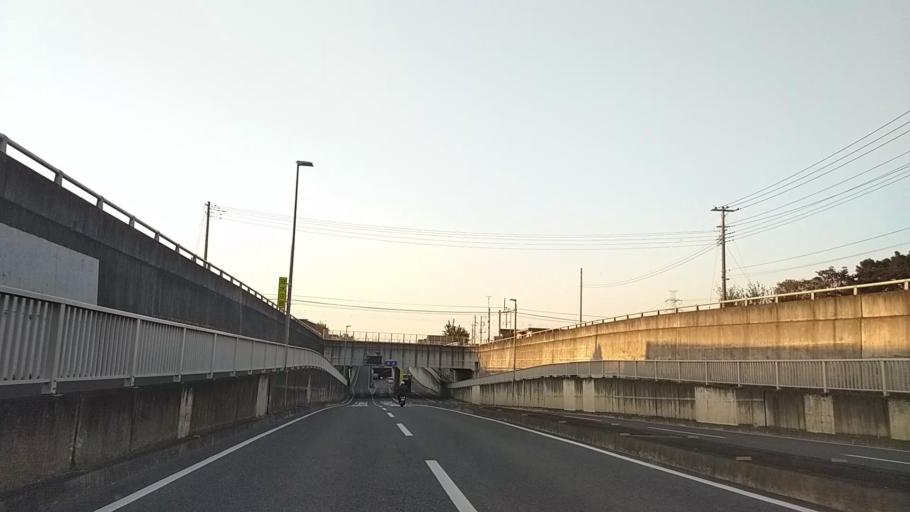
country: JP
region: Saitama
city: Sayama
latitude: 35.8661
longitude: 139.4248
